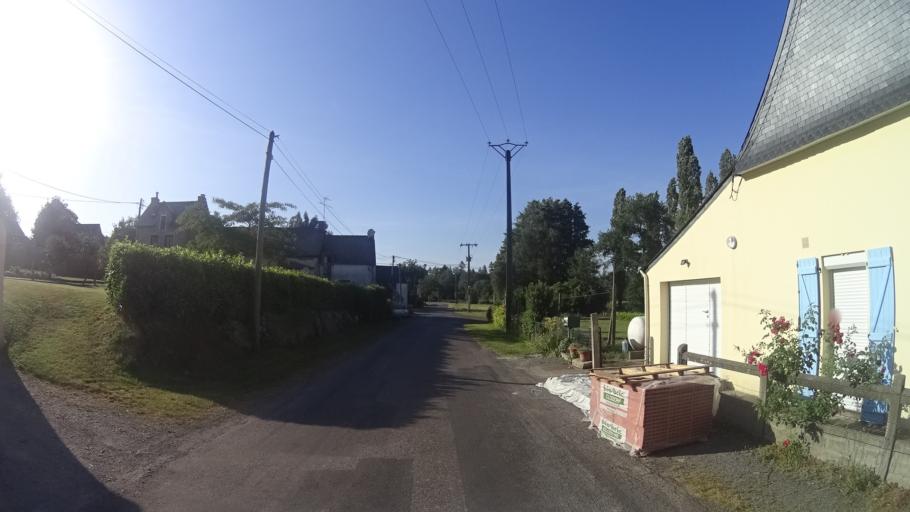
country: FR
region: Brittany
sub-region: Departement du Morbihan
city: Rieux
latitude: 47.6046
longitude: -2.1085
